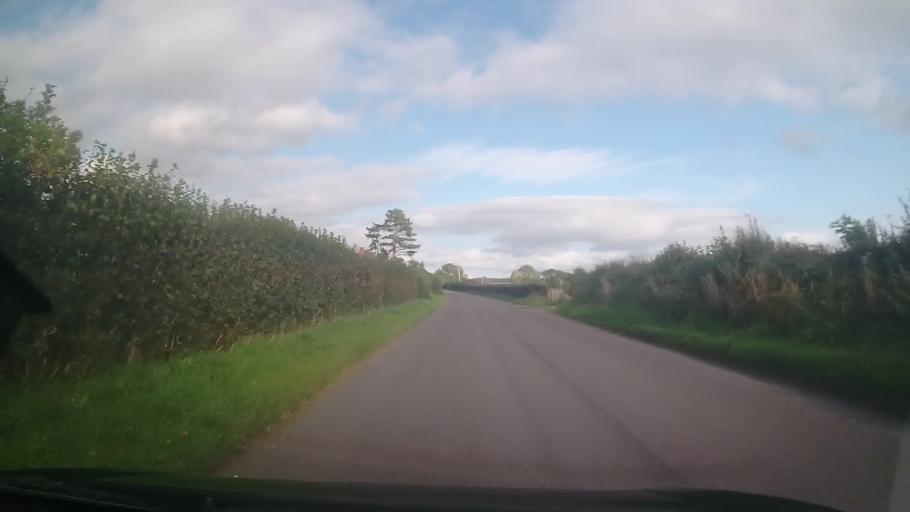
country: GB
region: England
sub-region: Shropshire
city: Craven Arms
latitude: 52.4295
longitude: -2.8868
